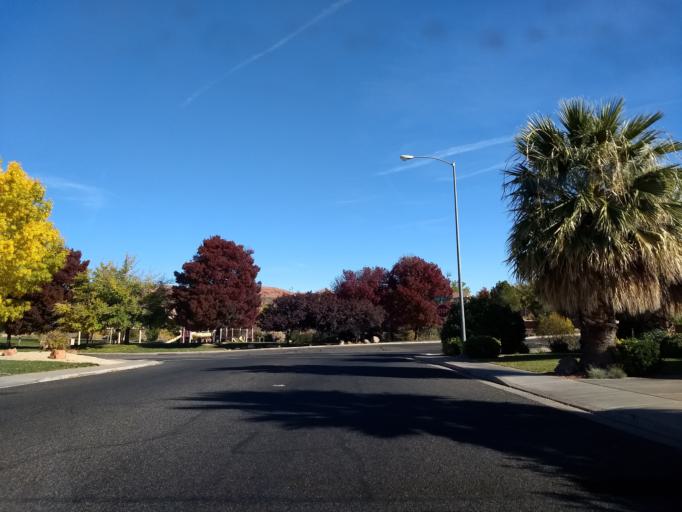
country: US
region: Utah
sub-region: Washington County
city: Santa Clara
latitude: 37.1294
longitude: -113.6156
